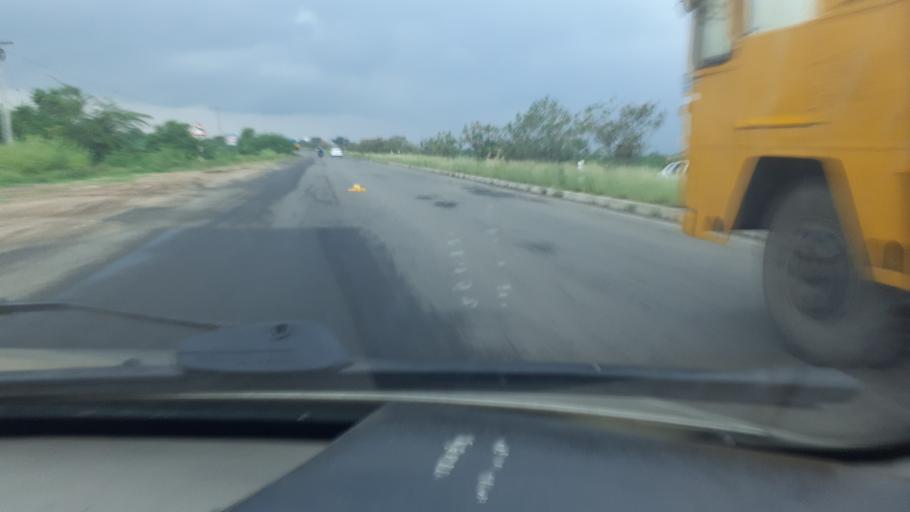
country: IN
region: Tamil Nadu
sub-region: Thoothukkudi
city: Kovilpatti
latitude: 9.1217
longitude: 77.8179
